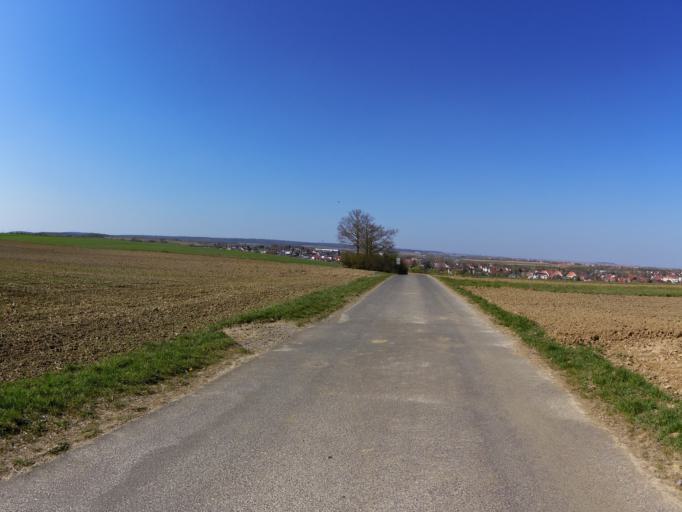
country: DE
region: Bavaria
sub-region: Regierungsbezirk Unterfranken
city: Kurnach
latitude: 49.8368
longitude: 10.0374
